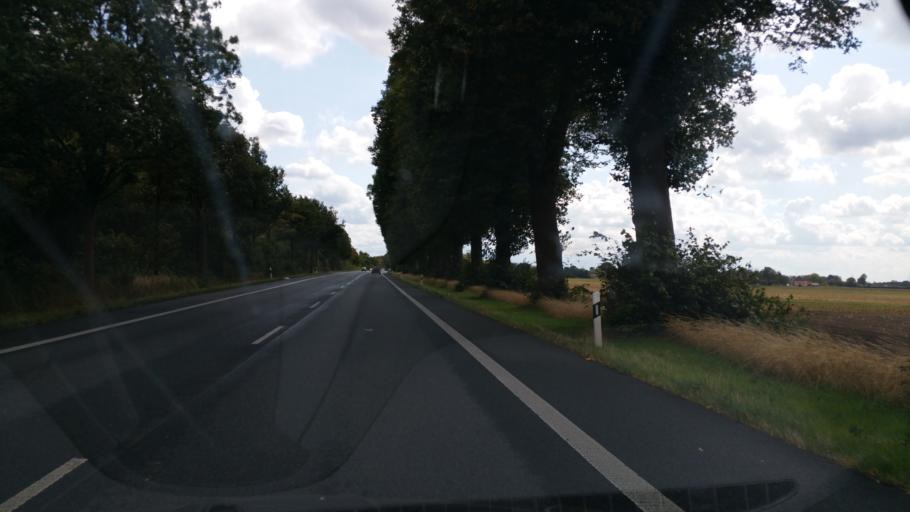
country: DE
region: North Rhine-Westphalia
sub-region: Regierungsbezirk Dusseldorf
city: Hamminkeln
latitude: 51.7595
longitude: 6.5854
